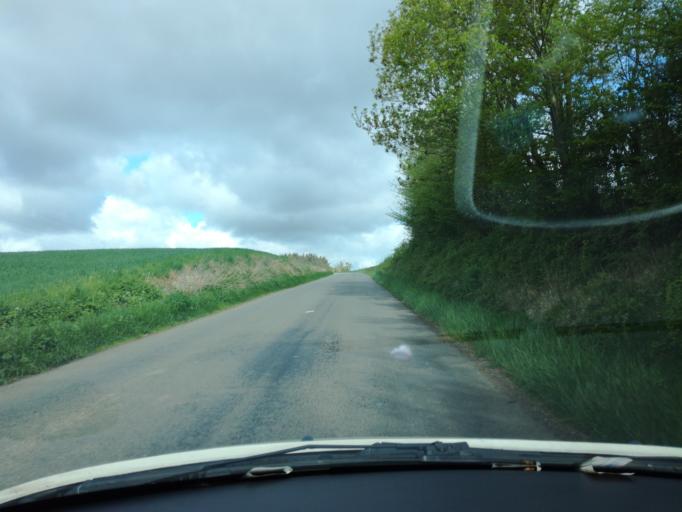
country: FR
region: Picardie
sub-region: Departement de la Somme
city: Poix-de-Picardie
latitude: 49.8171
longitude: 1.9796
